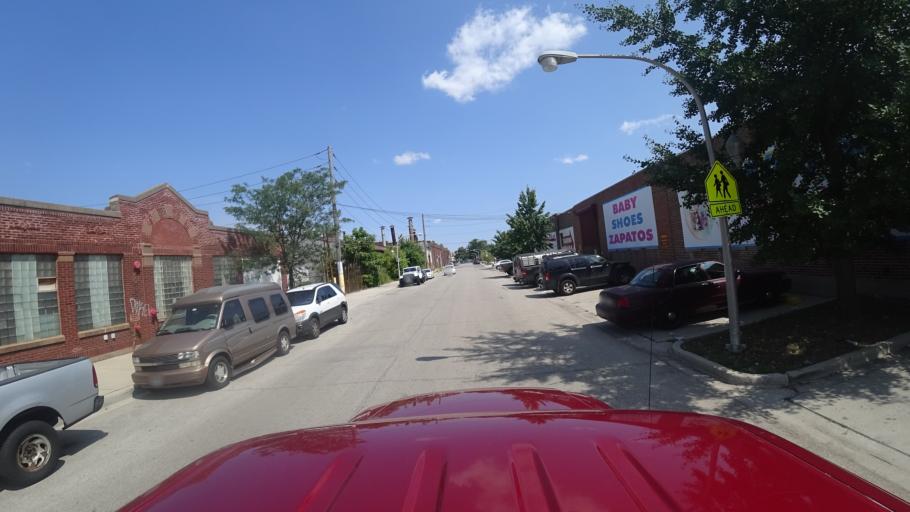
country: US
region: Illinois
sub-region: Cook County
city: Chicago
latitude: 41.8063
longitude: -87.6977
